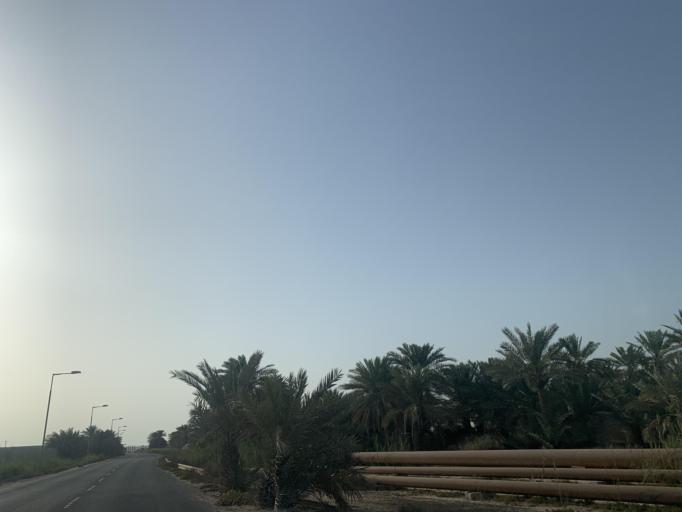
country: BH
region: Central Governorate
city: Madinat Hamad
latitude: 26.1780
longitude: 50.4562
